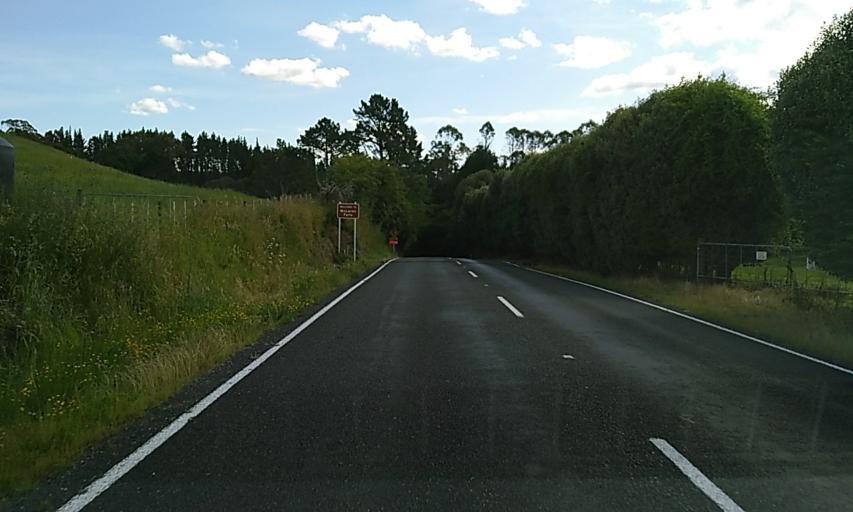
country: NZ
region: Bay of Plenty
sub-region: Tauranga City
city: Tauranga
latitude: -37.8034
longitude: 176.0433
